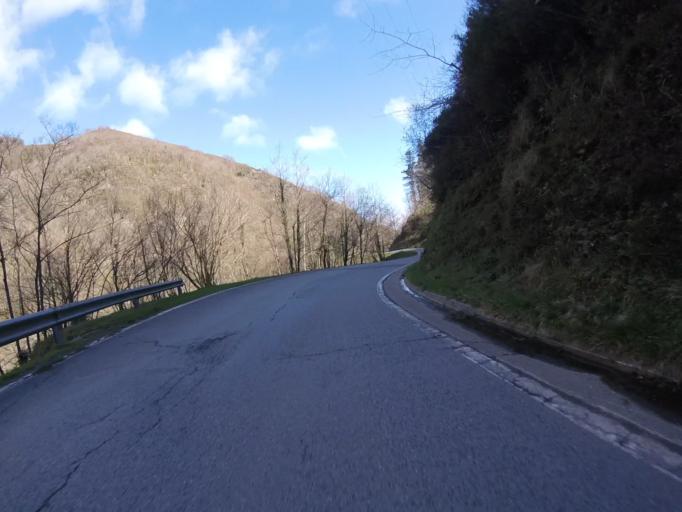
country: ES
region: Navarre
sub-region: Provincia de Navarra
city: Ezkurra
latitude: 43.1039
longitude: -1.8614
